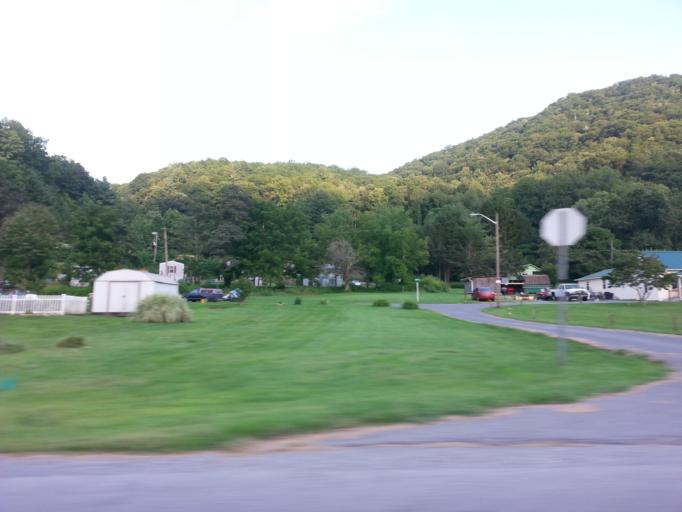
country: US
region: Tennessee
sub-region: Johnson County
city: Mountain City
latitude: 36.6263
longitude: -81.7897
